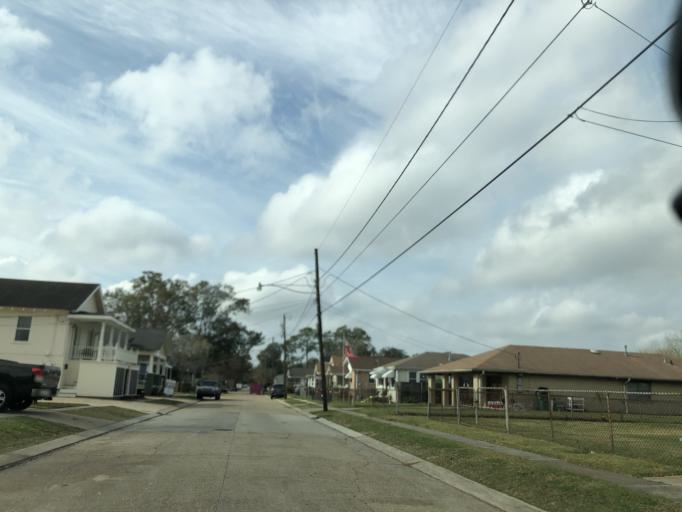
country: US
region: Louisiana
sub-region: Jefferson Parish
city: Metairie Terrace
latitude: 29.9775
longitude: -90.1628
